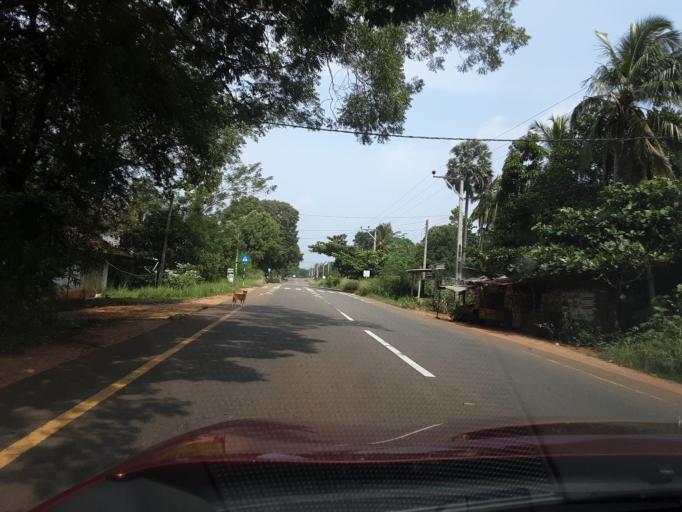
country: LK
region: North Central
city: Anuradhapura
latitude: 8.3309
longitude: 80.5011
